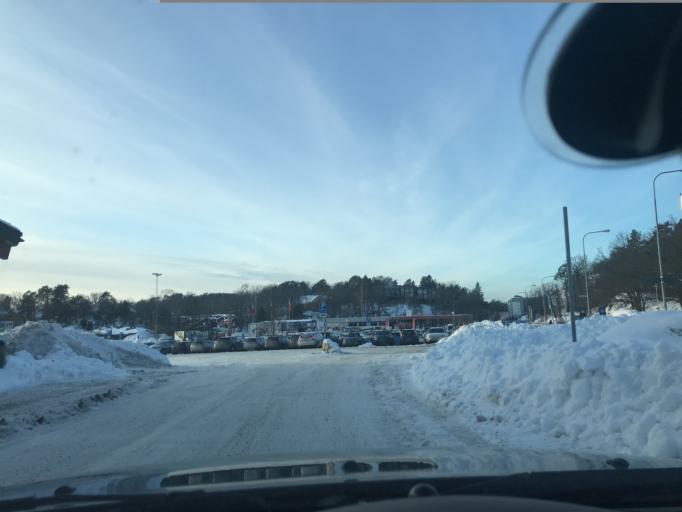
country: SE
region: Stockholm
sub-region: Varmdo Kommun
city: Gustavsberg
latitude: 59.3276
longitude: 18.3956
